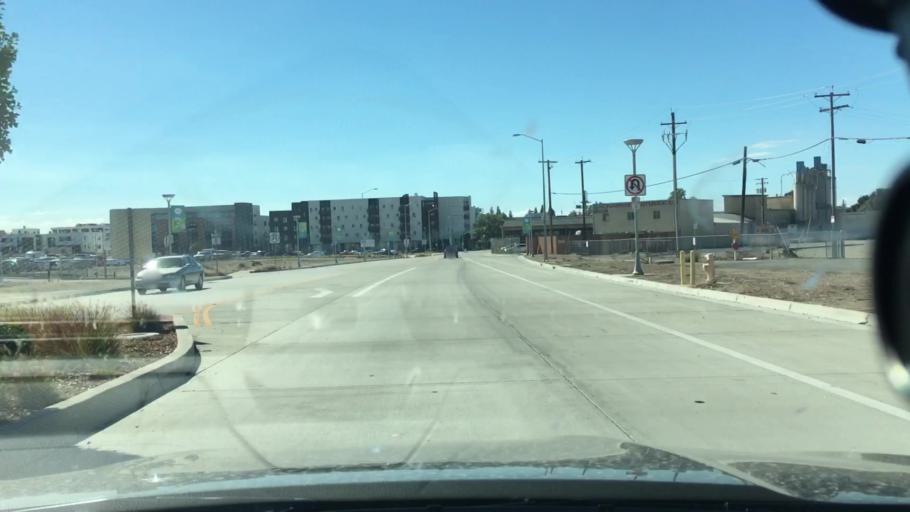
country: US
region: California
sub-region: Yolo County
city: West Sacramento
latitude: 38.5792
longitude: -121.5160
